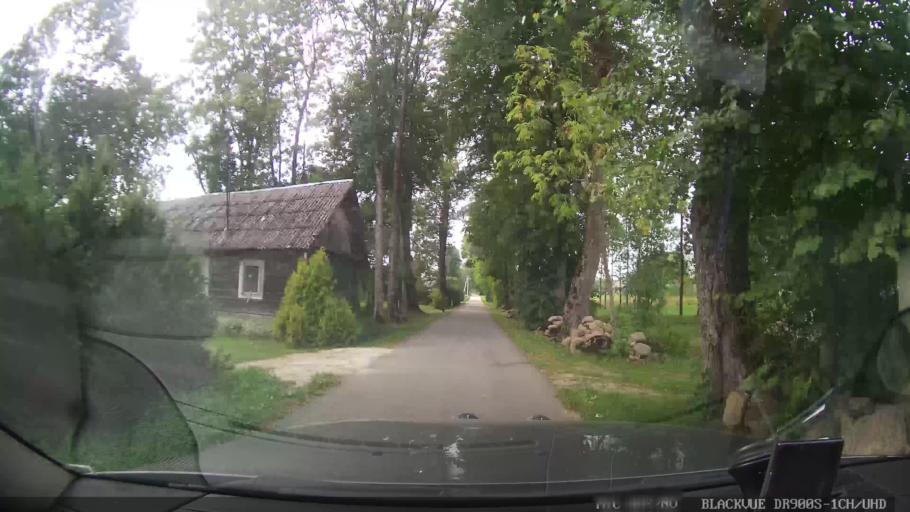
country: BY
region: Grodnenskaya
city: Ashmyany
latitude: 54.5328
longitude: 25.6650
